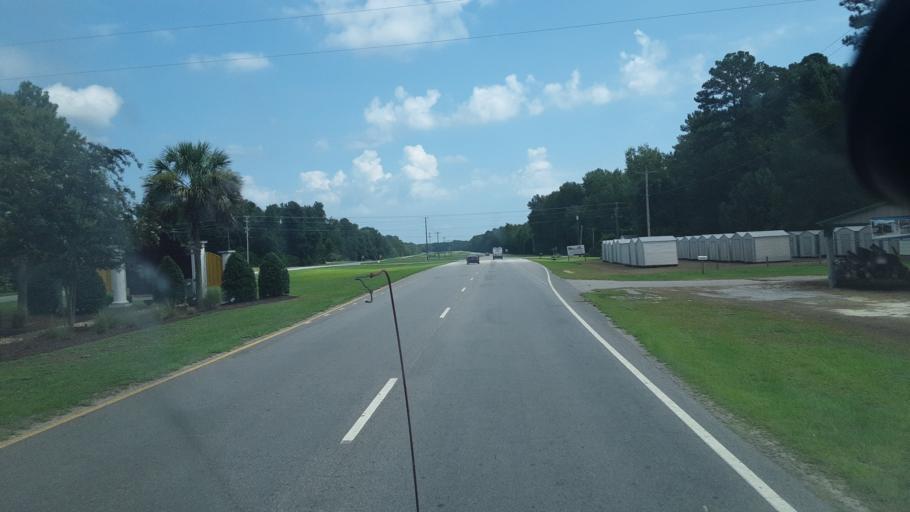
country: US
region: South Carolina
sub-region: Bamberg County
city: Bamberg
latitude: 33.3212
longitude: -81.0297
